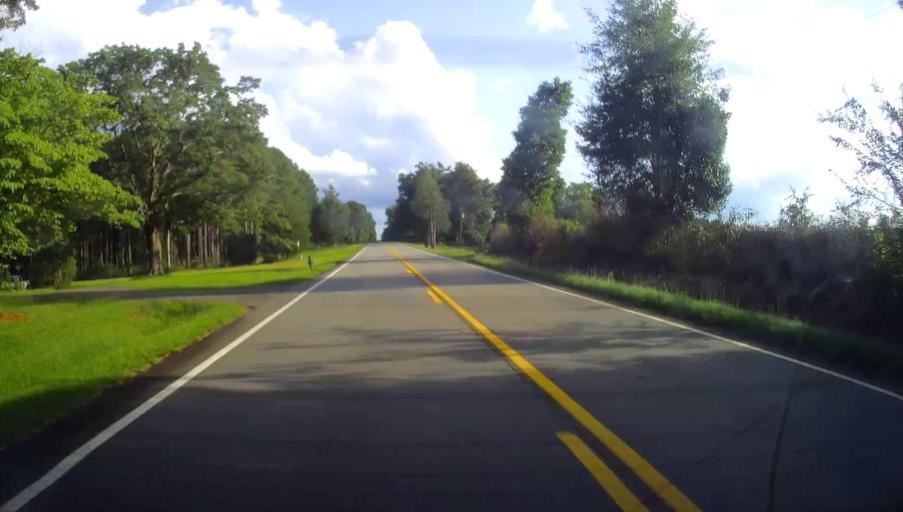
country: US
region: Georgia
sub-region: Monroe County
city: Forsyth
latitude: 32.8986
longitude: -83.9926
